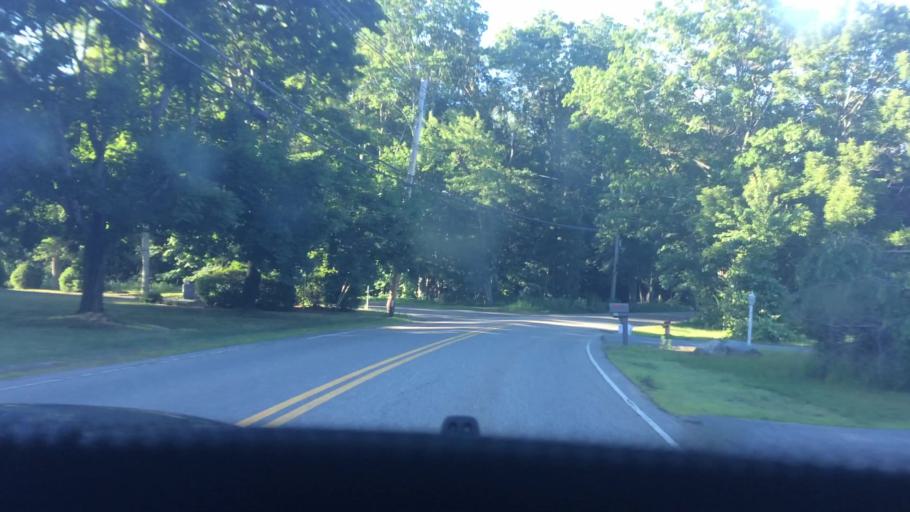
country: US
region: Massachusetts
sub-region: Essex County
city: Andover
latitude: 42.6422
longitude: -71.0872
